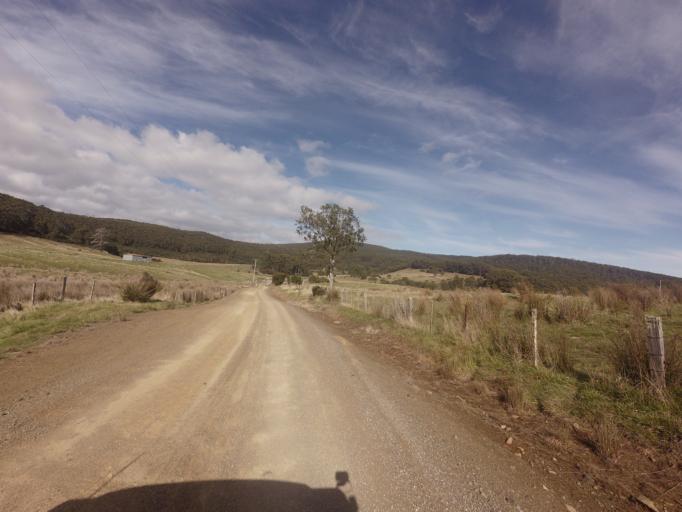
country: AU
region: Tasmania
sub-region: Clarence
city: Sandford
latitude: -43.1887
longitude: 147.7749
